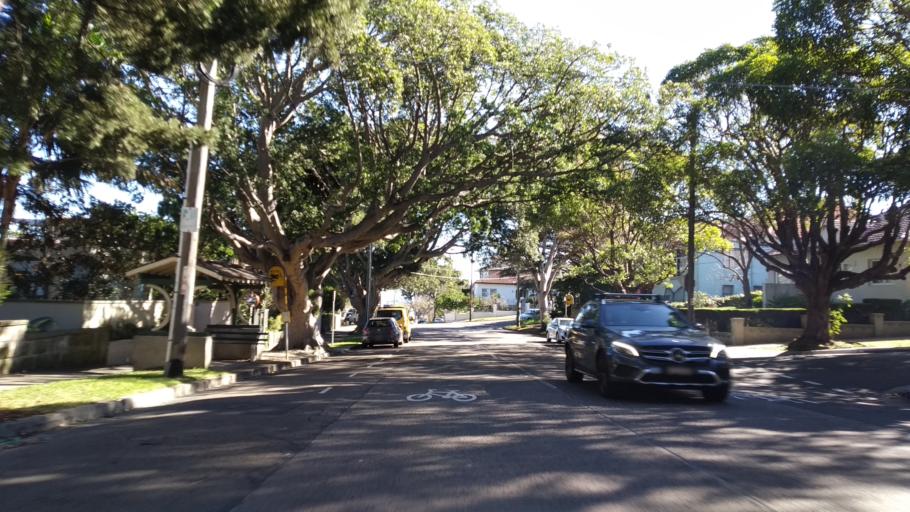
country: AU
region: New South Wales
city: Edgecliff
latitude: -33.8851
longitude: 151.2555
